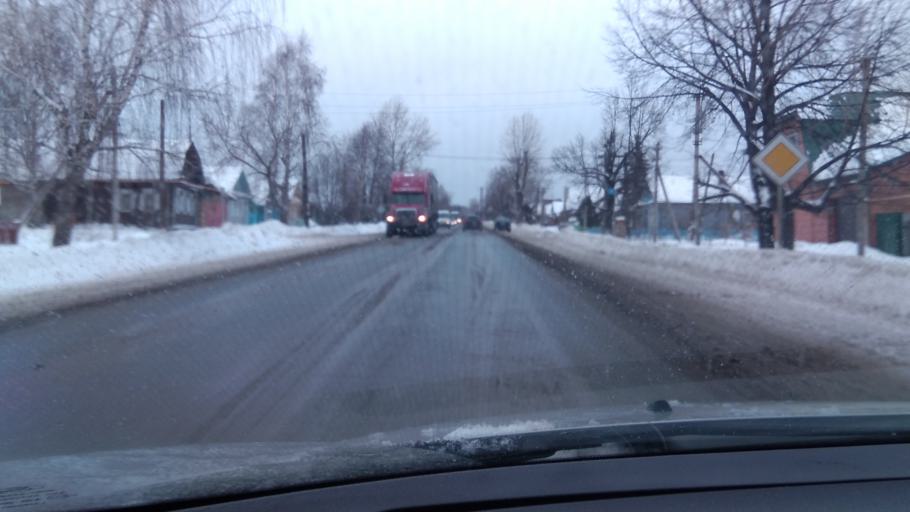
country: RU
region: Sverdlovsk
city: Nikolo-Pavlovskoye
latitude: 57.7885
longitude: 60.0555
